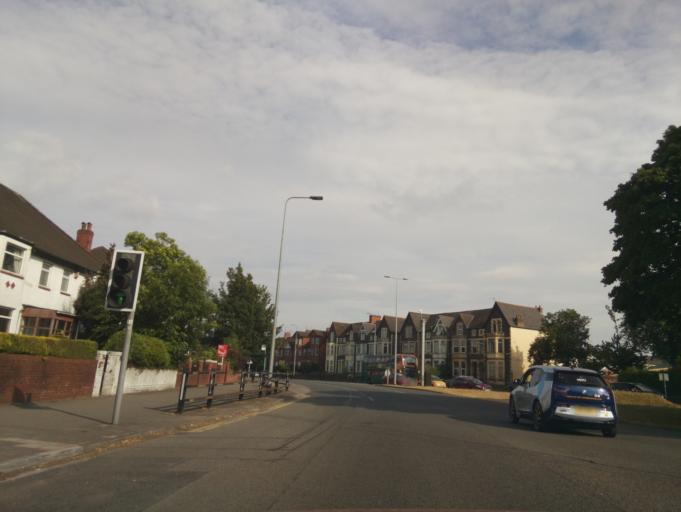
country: GB
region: Wales
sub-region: Cardiff
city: Cardiff
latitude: 51.4918
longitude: -3.1545
